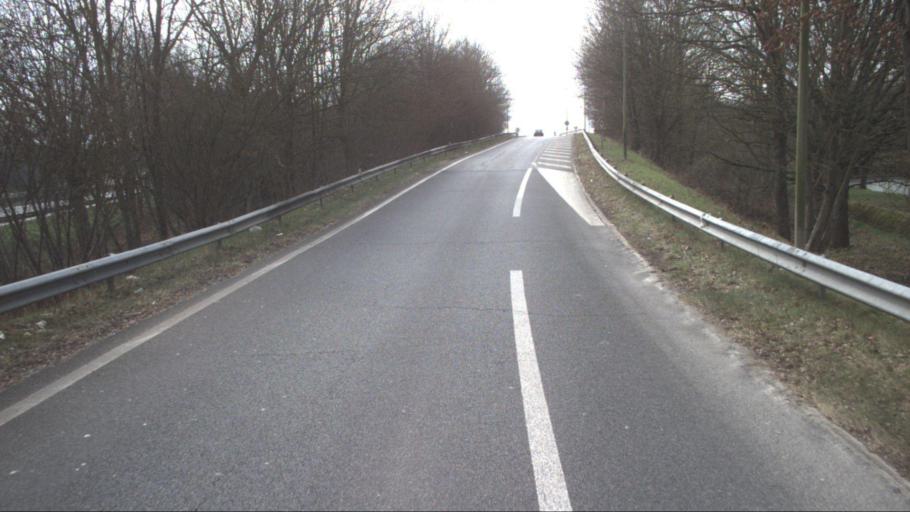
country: FR
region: Ile-de-France
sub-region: Departement des Yvelines
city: Rambouillet
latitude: 48.6218
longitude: 1.8306
